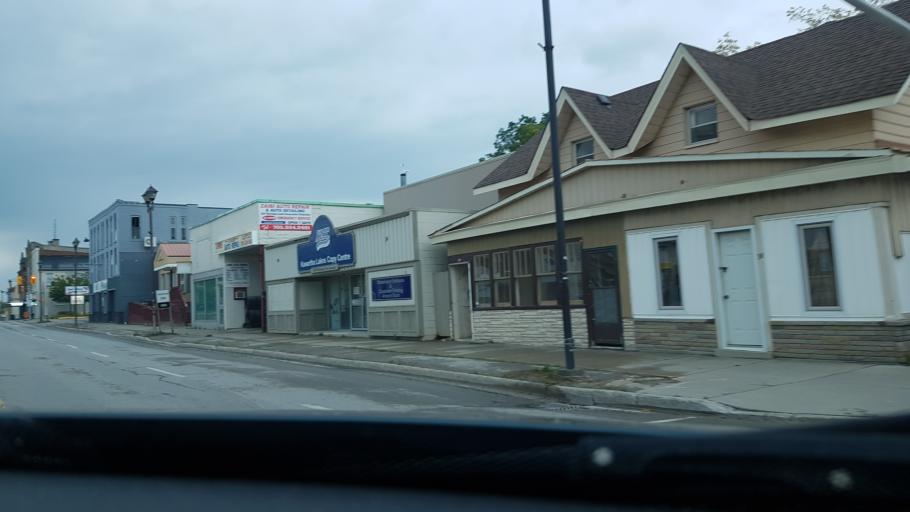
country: CA
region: Ontario
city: Omemee
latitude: 44.3543
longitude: -78.7343
